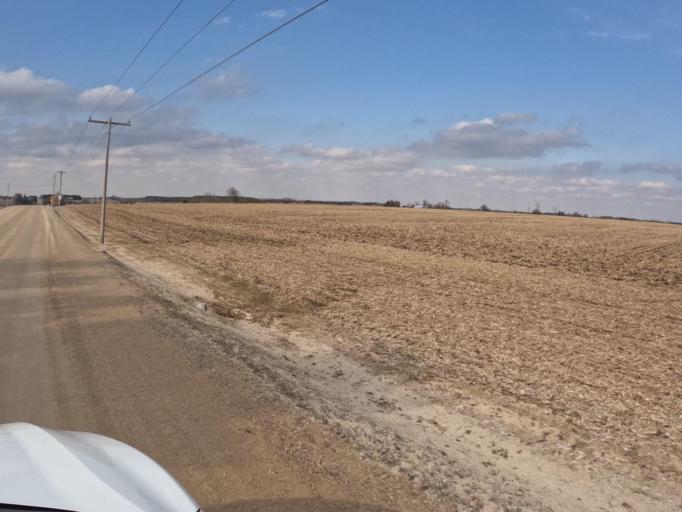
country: CA
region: Ontario
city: Orangeville
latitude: 43.8867
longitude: -80.2982
